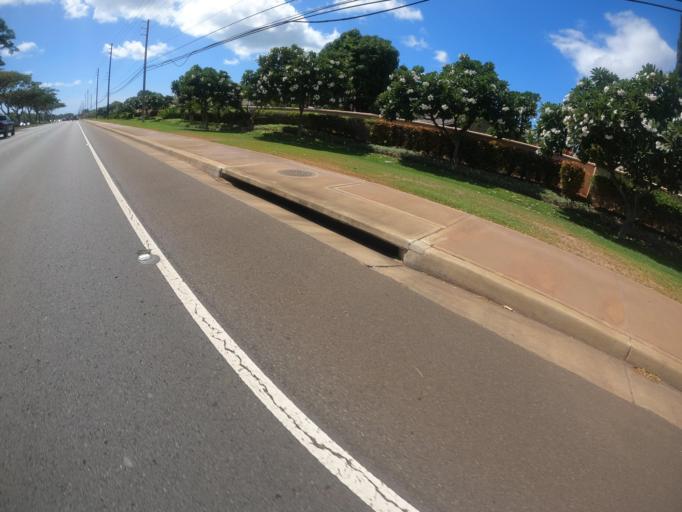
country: US
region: Hawaii
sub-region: Honolulu County
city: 'Ewa Gentry
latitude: 21.3452
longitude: -158.0263
